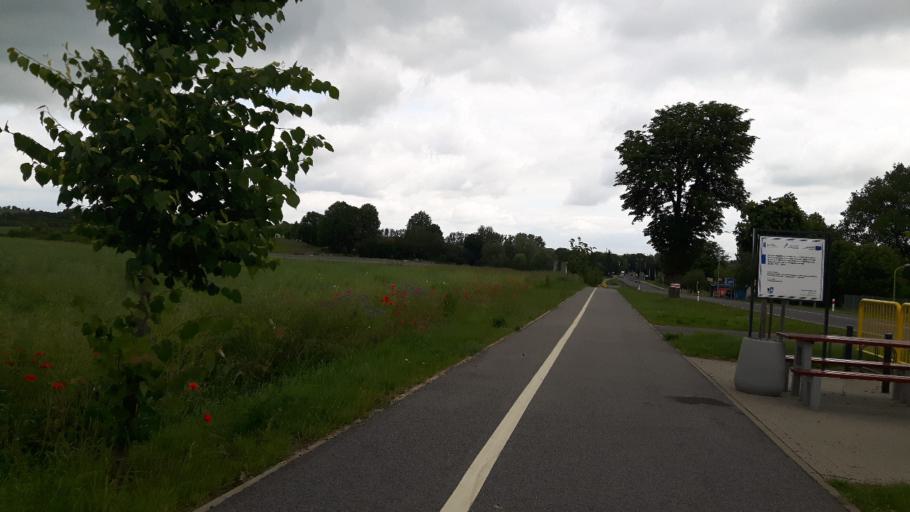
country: PL
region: West Pomeranian Voivodeship
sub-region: Powiat policki
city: Kolbaskowo
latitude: 53.3330
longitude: 14.4317
